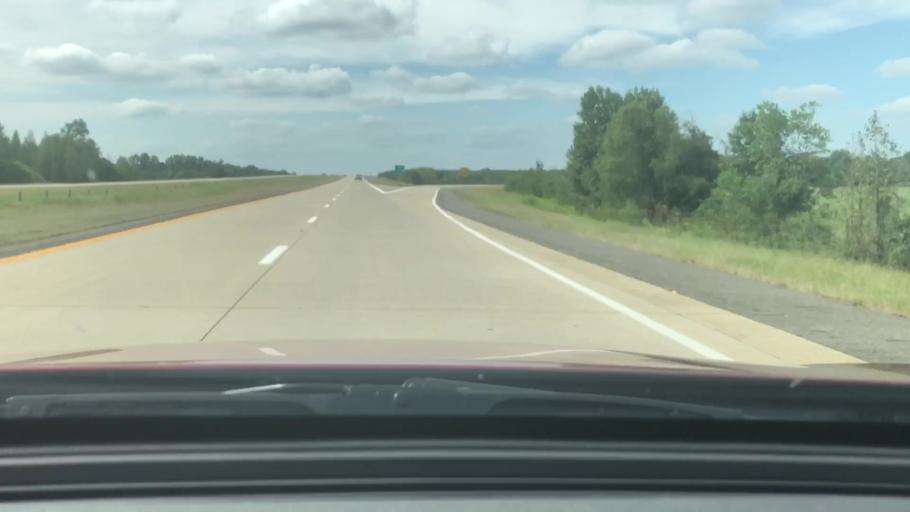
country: US
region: Texas
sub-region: Bowie County
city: Texarkana
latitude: 33.2469
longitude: -93.8799
